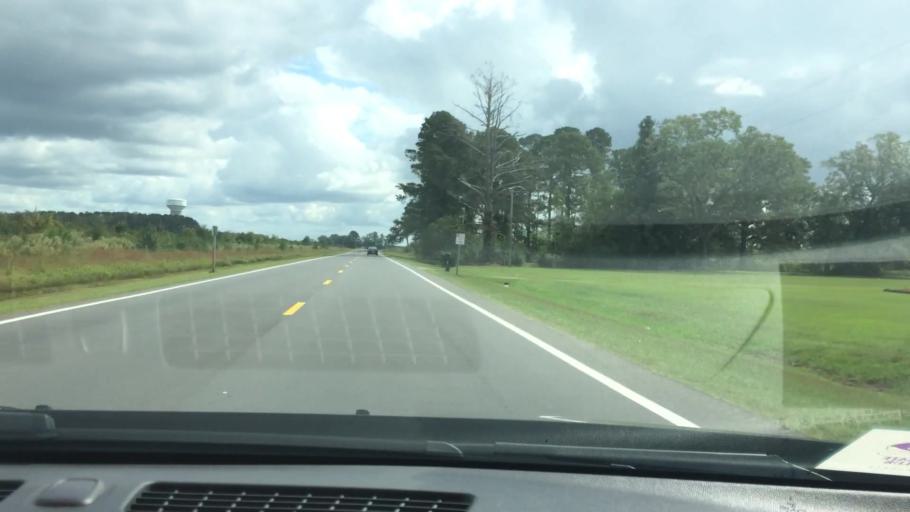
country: US
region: North Carolina
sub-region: Pitt County
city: Farmville
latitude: 35.5549
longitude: -77.5538
